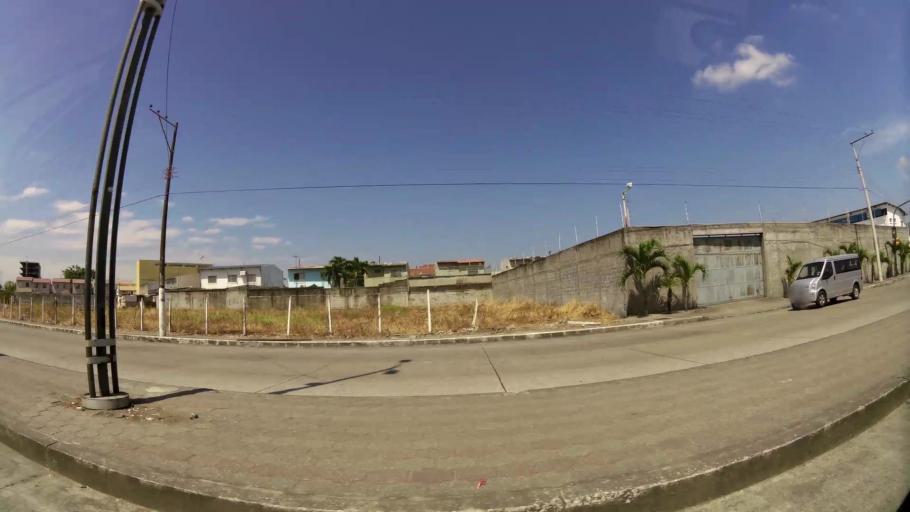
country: EC
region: Guayas
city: Guayaquil
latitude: -2.1298
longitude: -79.9286
